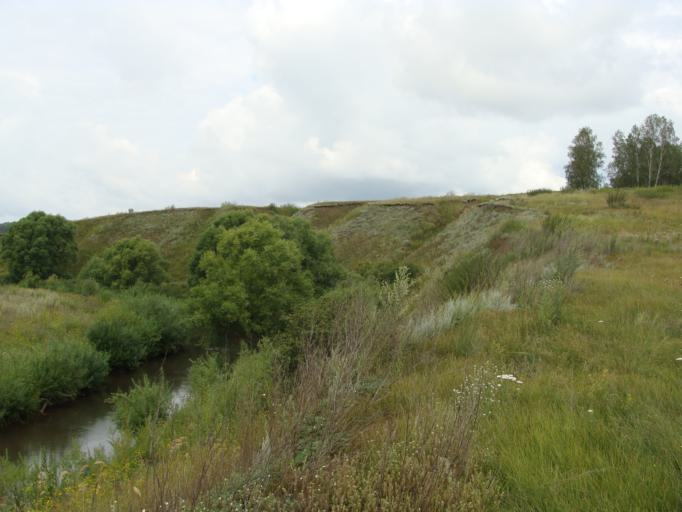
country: RU
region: Altai Krai
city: Troitskoye
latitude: 53.0857
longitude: 84.9768
